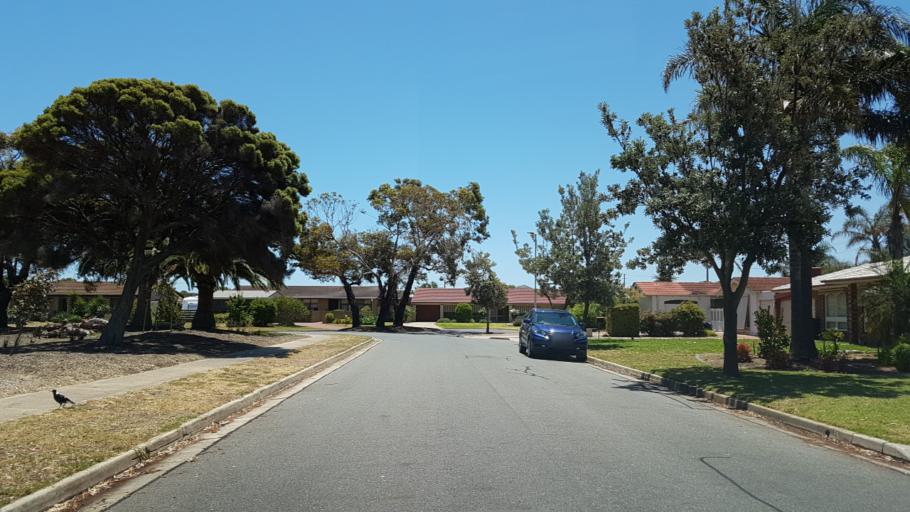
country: AU
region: South Australia
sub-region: Charles Sturt
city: West Lakes Shore
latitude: -34.8554
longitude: 138.4873
